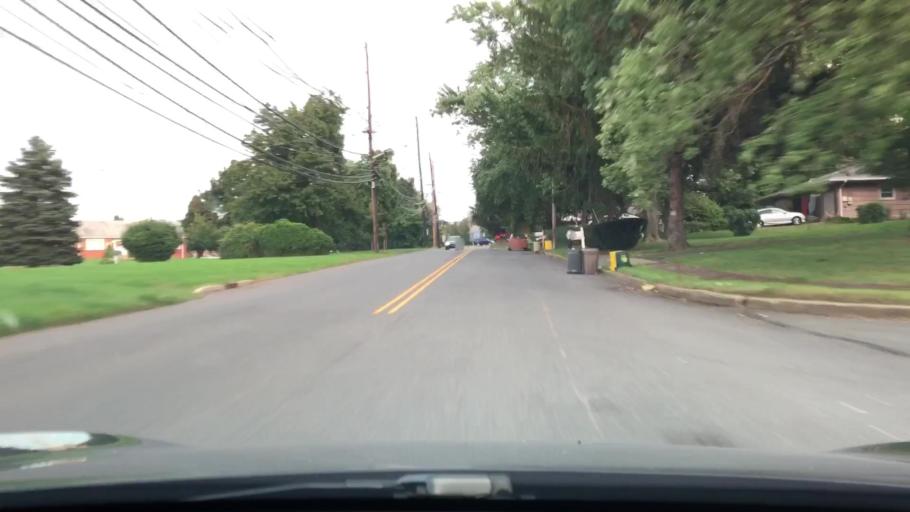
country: US
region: New Jersey
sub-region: Mercer County
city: Ewing
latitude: 40.2848
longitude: -74.7652
